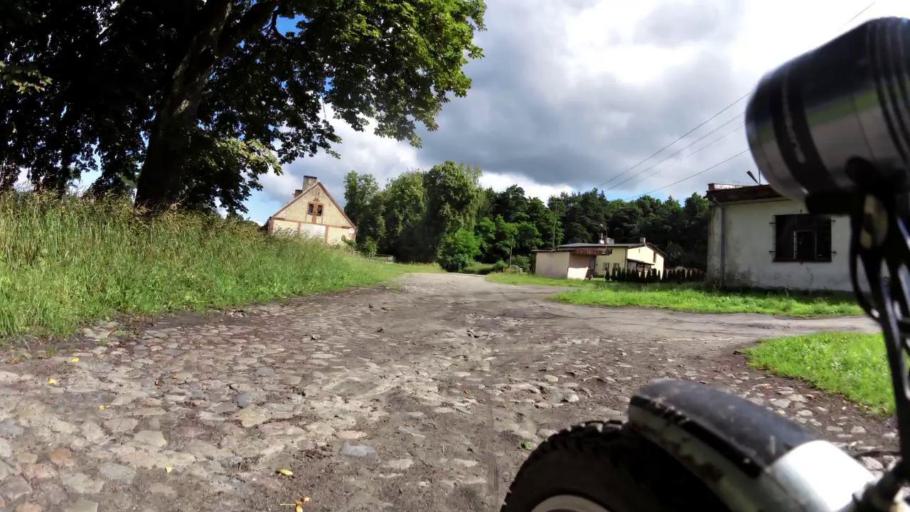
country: PL
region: West Pomeranian Voivodeship
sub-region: Powiat swidwinski
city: Rabino
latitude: 53.8121
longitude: 15.8916
